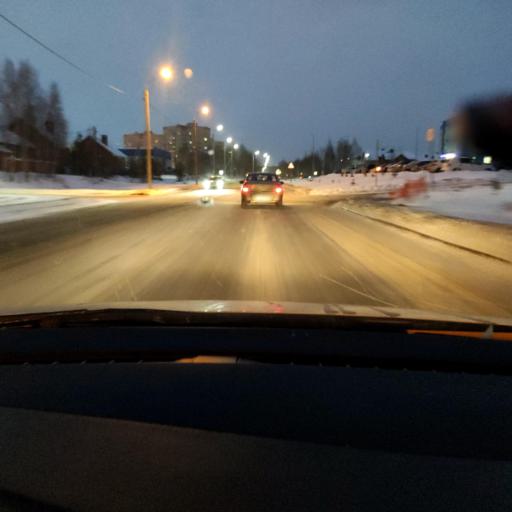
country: RU
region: Tatarstan
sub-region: Zelenodol'skiy Rayon
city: Zelenodolsk
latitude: 55.8664
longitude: 48.5635
